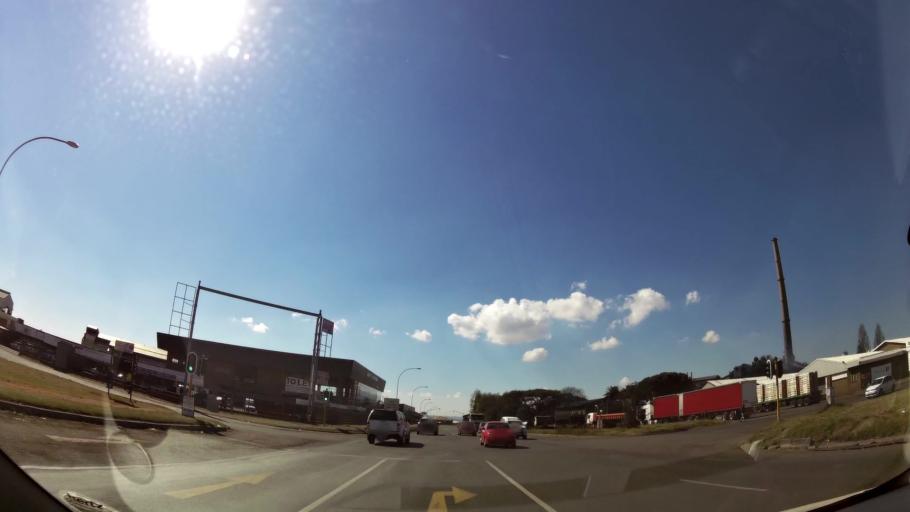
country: ZA
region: Mpumalanga
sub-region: Nkangala District Municipality
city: Witbank
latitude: -25.8634
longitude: 29.2220
